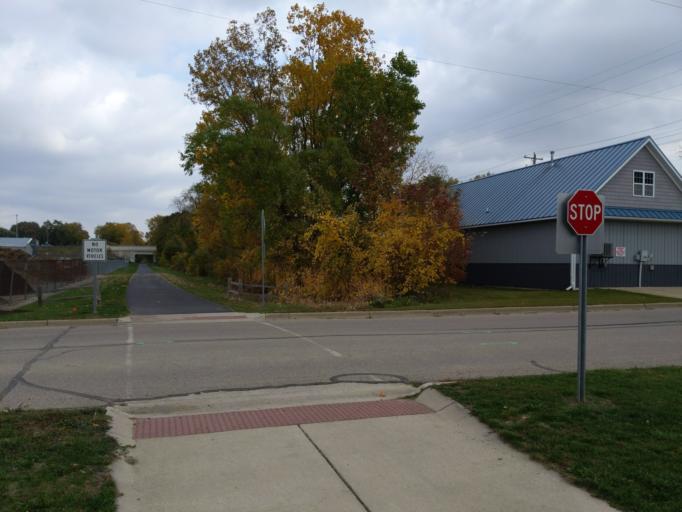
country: US
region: Michigan
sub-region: Clinton County
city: Saint Johns
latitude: 43.0049
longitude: -84.5541
